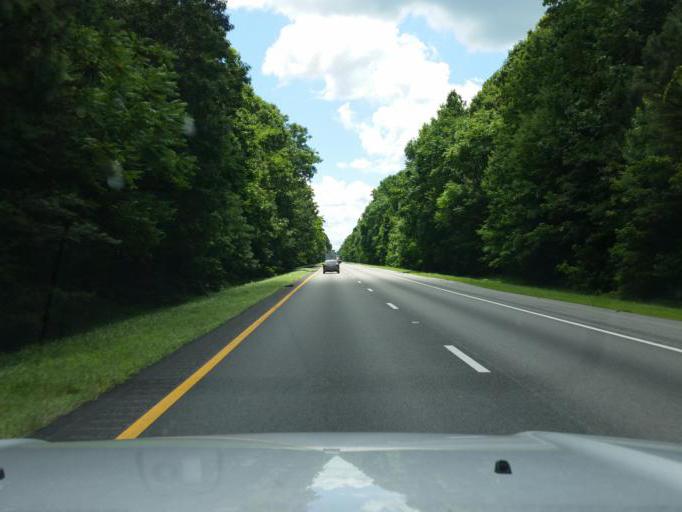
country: US
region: Virginia
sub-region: James City County
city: Williamsburg
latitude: 37.3977
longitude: -76.7768
